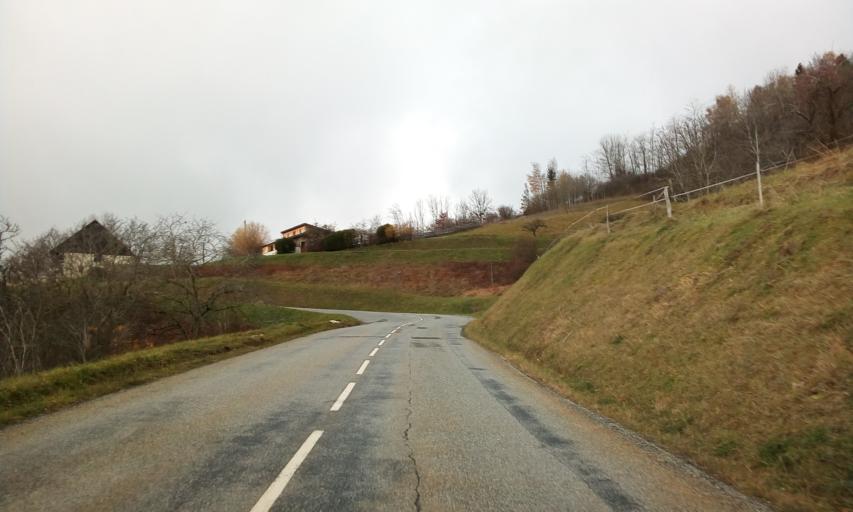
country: FR
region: Rhone-Alpes
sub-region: Departement de la Savoie
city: Barby
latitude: 45.5852
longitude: 6.0386
